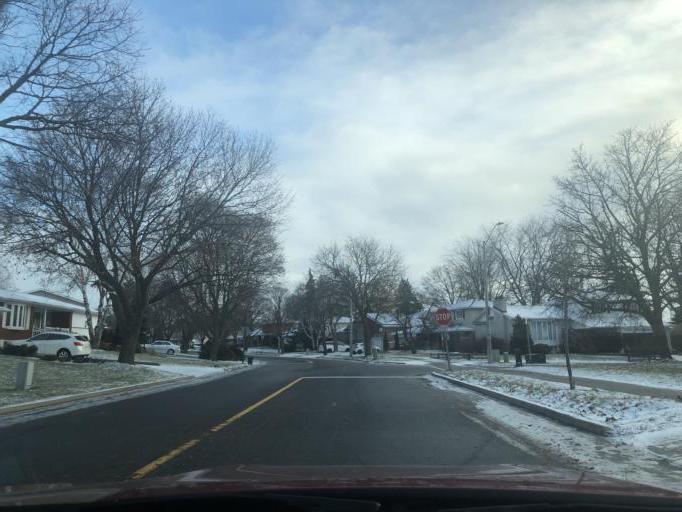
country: CA
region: Ontario
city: Markham
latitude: 43.8762
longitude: -79.2425
